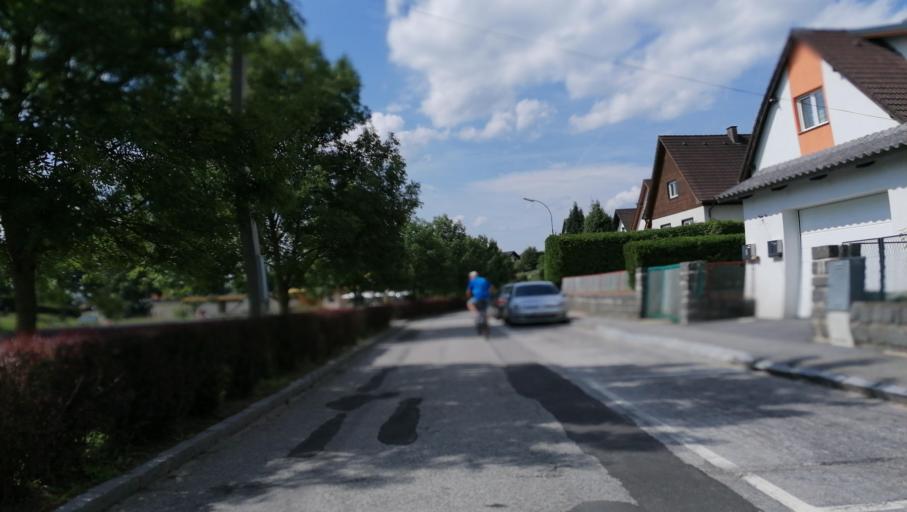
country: AT
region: Lower Austria
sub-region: Politischer Bezirk Gmund
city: Schrems
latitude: 48.7952
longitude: 15.0799
